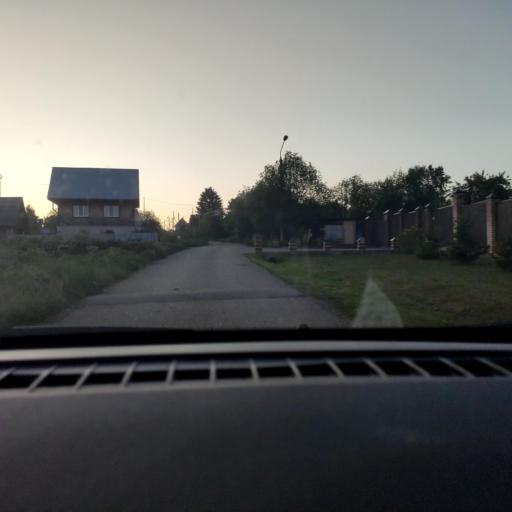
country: RU
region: Perm
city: Ferma
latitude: 57.9859
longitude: 56.3781
